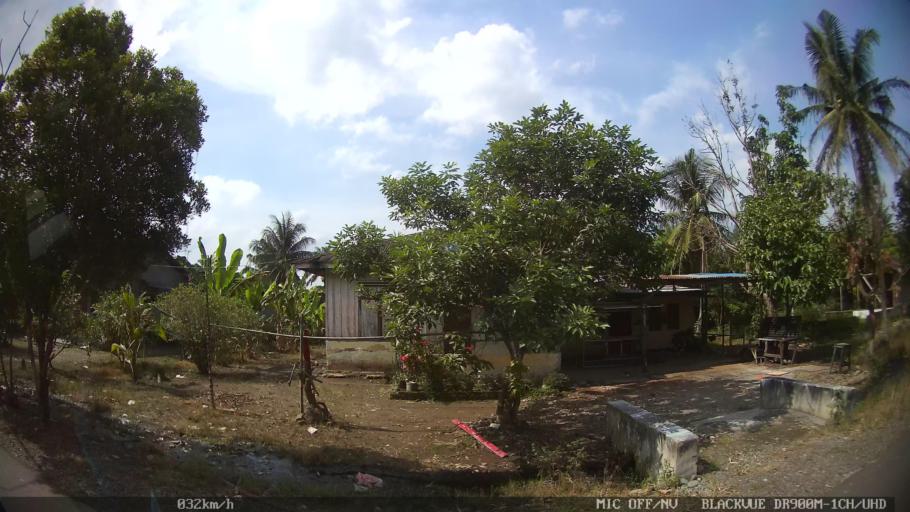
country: ID
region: North Sumatra
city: Binjai
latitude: 3.6354
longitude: 98.5191
